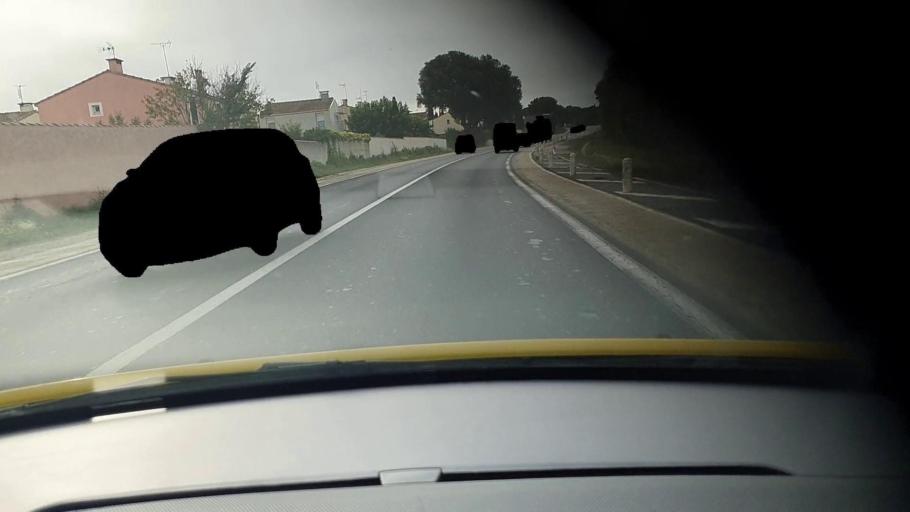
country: FR
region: Languedoc-Roussillon
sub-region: Departement du Gard
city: Caissargues
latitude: 43.7882
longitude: 4.3891
